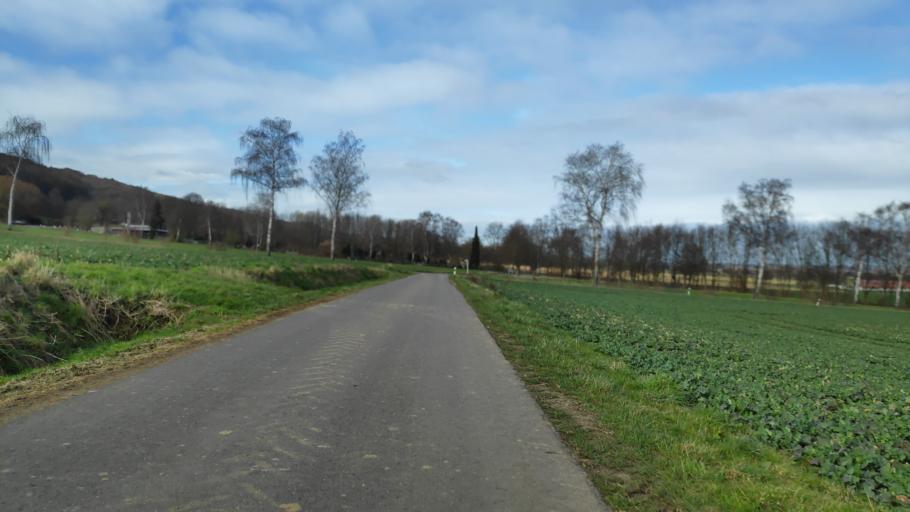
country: DE
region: North Rhine-Westphalia
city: Bad Oeynhausen
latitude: 52.2650
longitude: 8.8208
